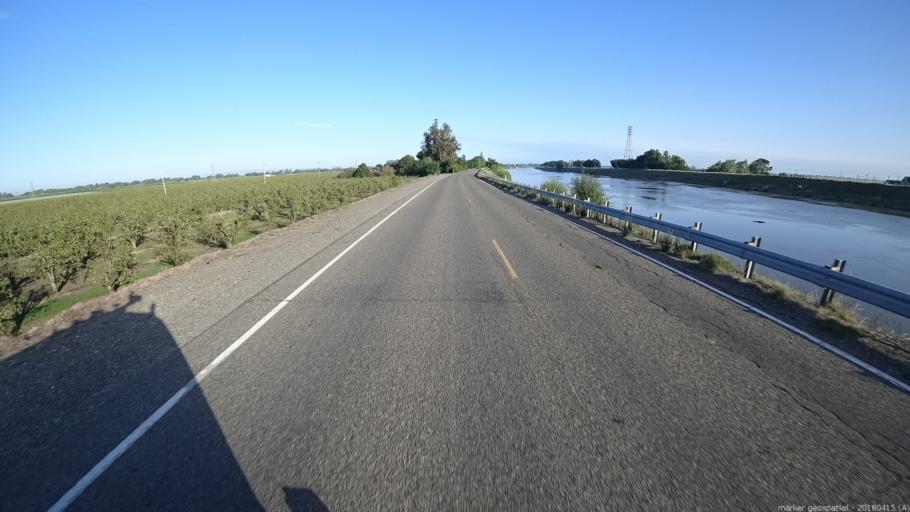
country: US
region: California
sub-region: Sacramento County
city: Walnut Grove
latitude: 38.2897
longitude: -121.5604
